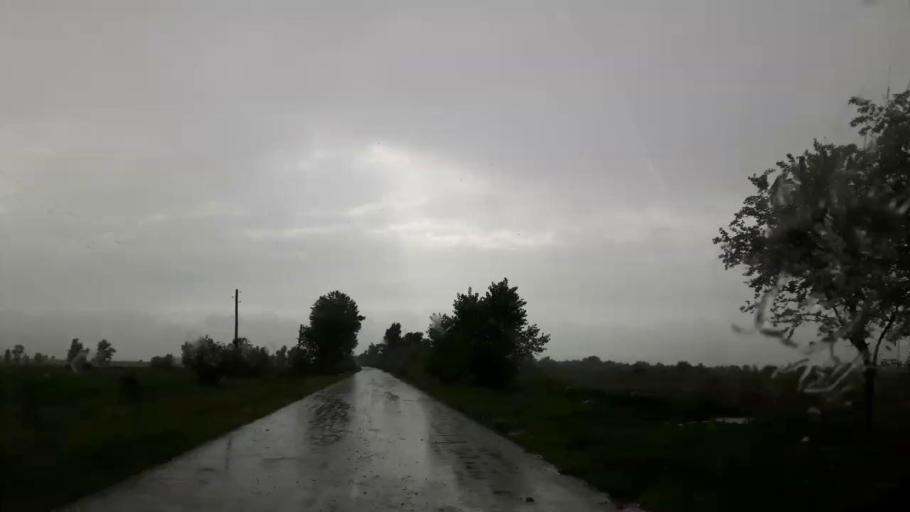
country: GE
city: Agara
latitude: 42.0140
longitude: 43.7999
